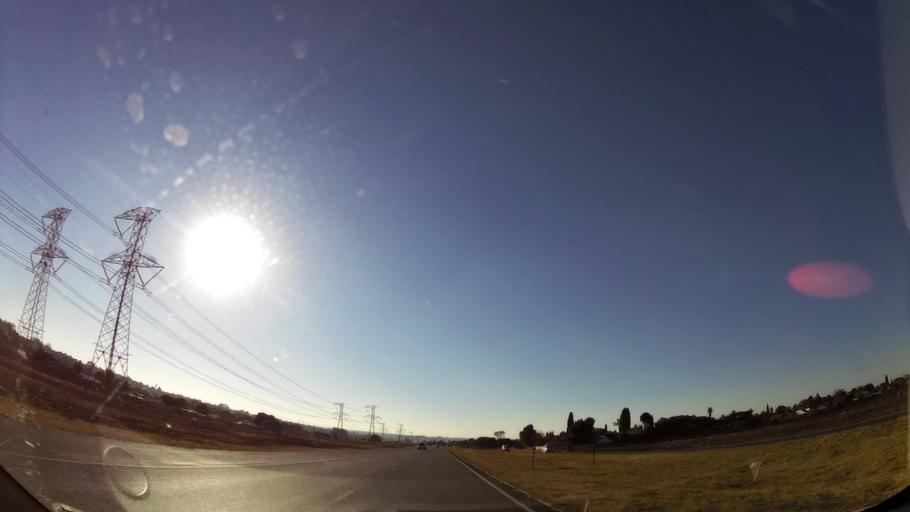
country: ZA
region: Gauteng
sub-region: City of Johannesburg Metropolitan Municipality
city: Modderfontein
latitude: -26.0885
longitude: 28.1962
